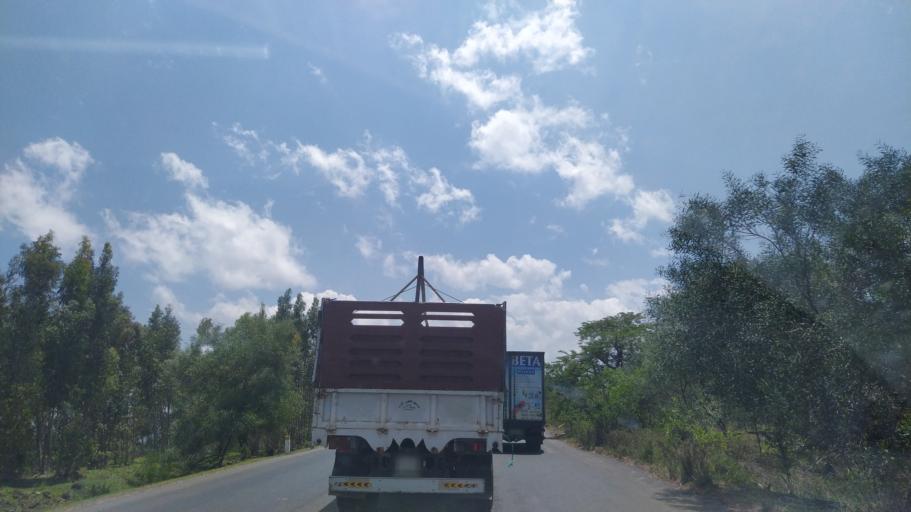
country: ET
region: Southern Nations, Nationalities, and People's Region
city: Butajira
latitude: 7.7783
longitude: 38.1382
